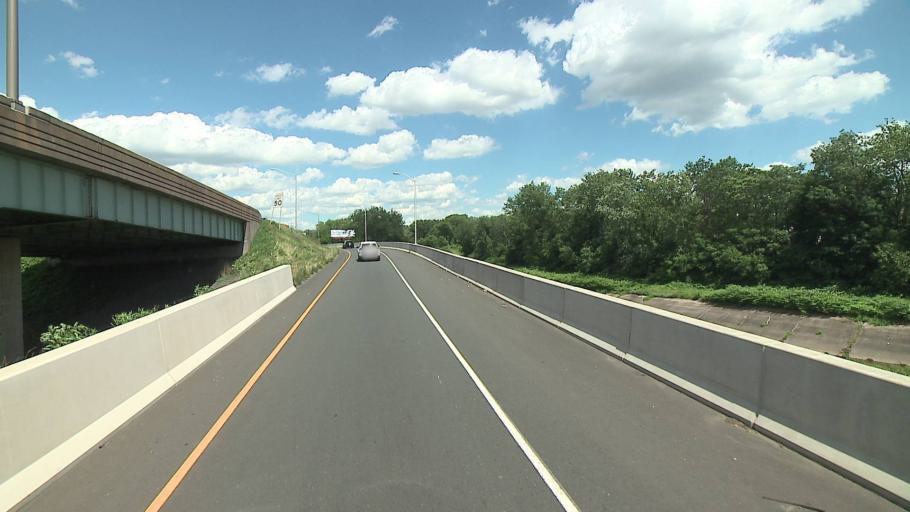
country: US
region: Connecticut
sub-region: Hartford County
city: Hartford
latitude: 41.7494
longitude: -72.7058
